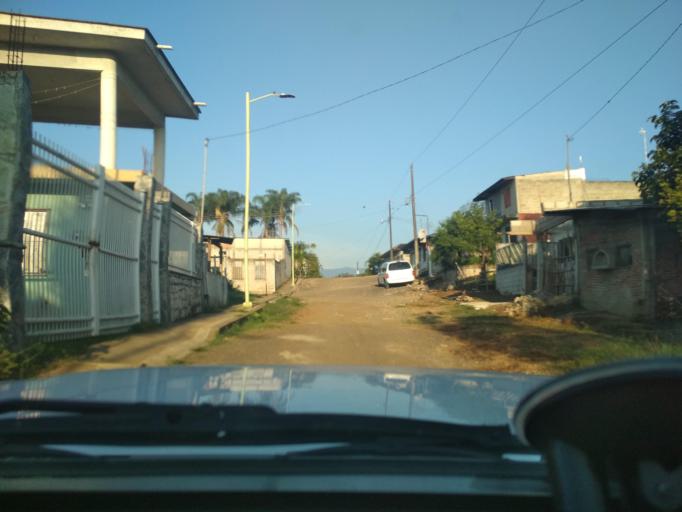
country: MX
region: Veracruz
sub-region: Fortin
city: Fraccionamiento Villas de la Llave
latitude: 18.9189
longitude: -96.9976
